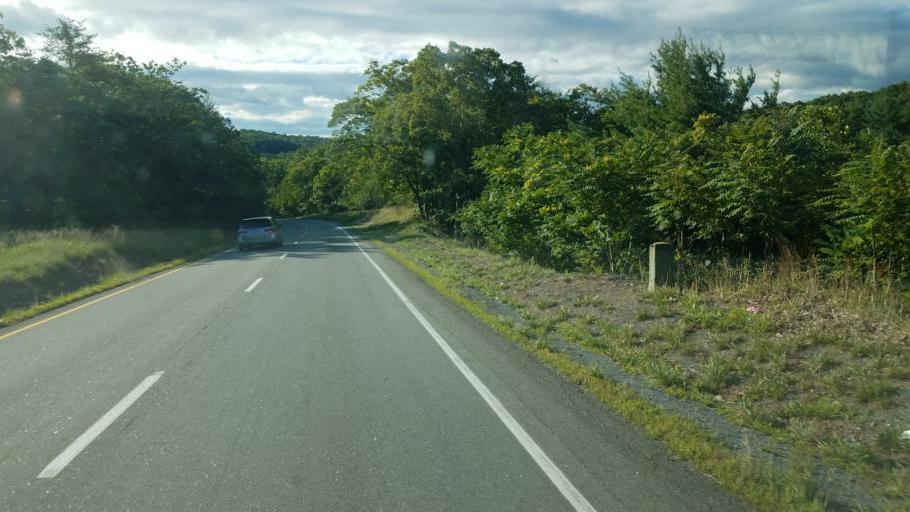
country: US
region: Virginia
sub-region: Frederick County
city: Shawnee Land
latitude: 39.3056
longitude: -78.2857
